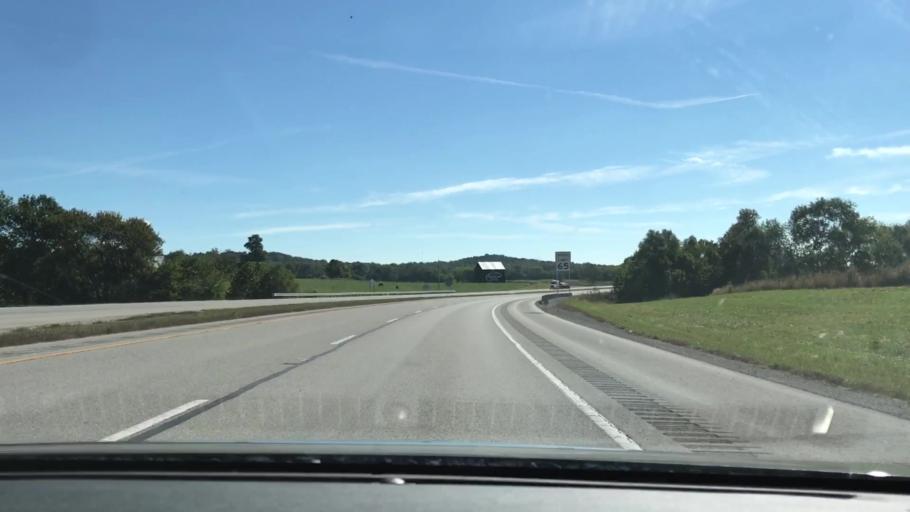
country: US
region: Kentucky
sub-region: Todd County
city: Elkton
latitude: 36.8238
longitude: -87.1498
